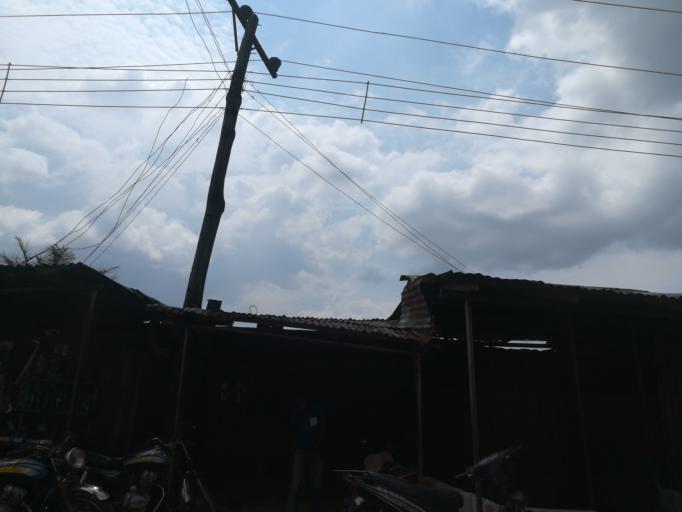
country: NG
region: Rivers
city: Okrika
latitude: 4.7271
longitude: 7.1546
